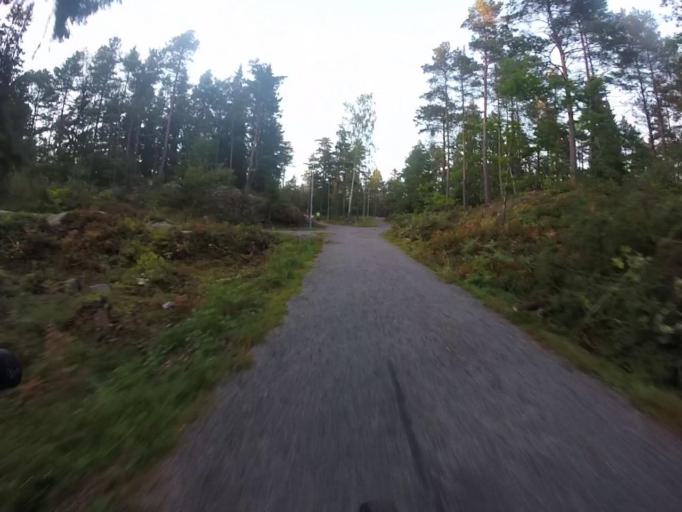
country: SE
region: Vaestra Goetaland
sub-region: Trollhattan
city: Trollhattan
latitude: 58.2962
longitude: 12.2695
